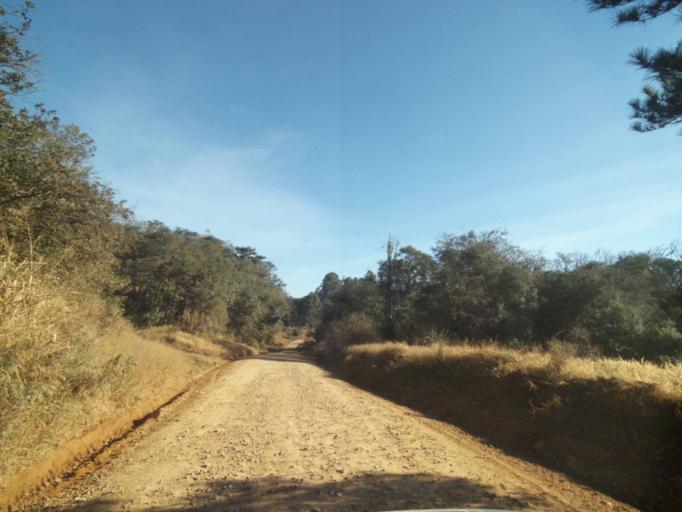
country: BR
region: Parana
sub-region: Tibagi
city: Tibagi
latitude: -24.5230
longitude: -50.5047
